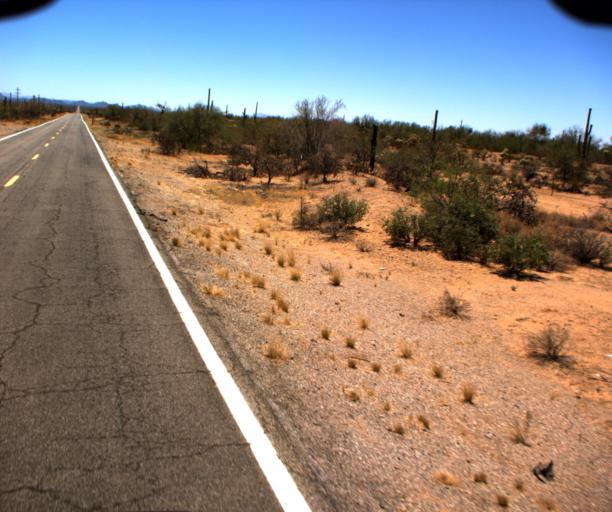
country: US
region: Arizona
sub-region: Pima County
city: Sells
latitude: 32.1127
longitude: -112.0757
